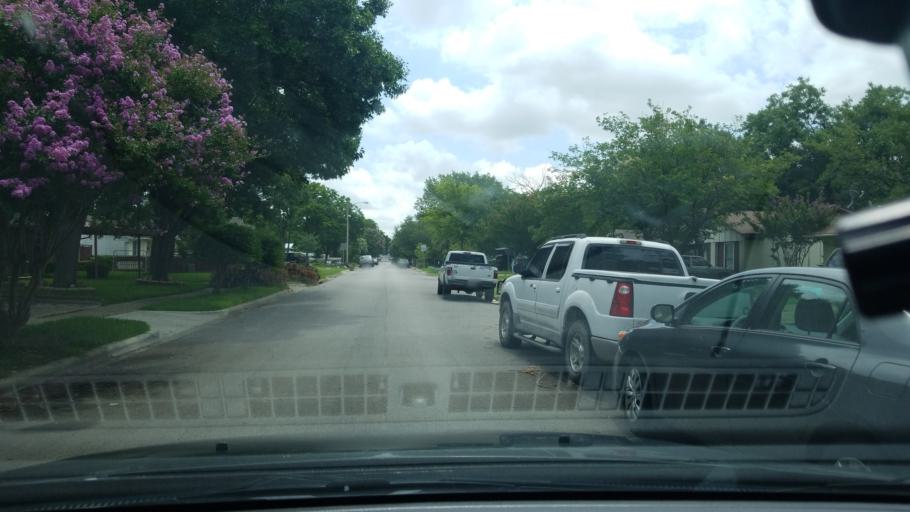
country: US
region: Texas
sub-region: Dallas County
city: Mesquite
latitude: 32.8133
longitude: -96.6713
